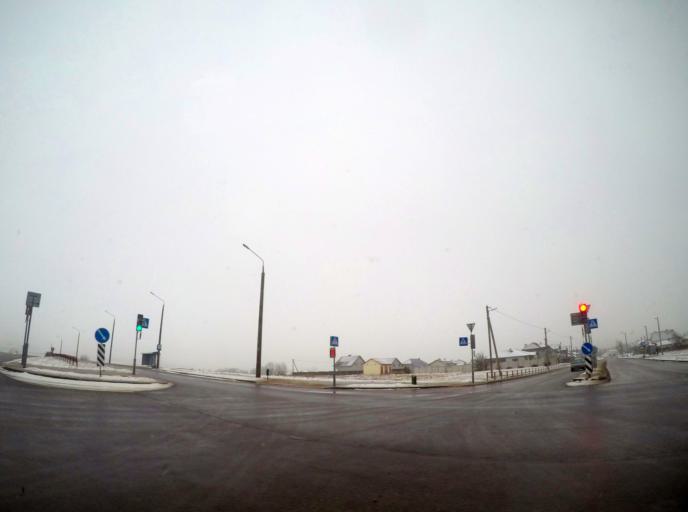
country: BY
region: Grodnenskaya
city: Hrodna
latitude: 53.6210
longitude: 23.8222
